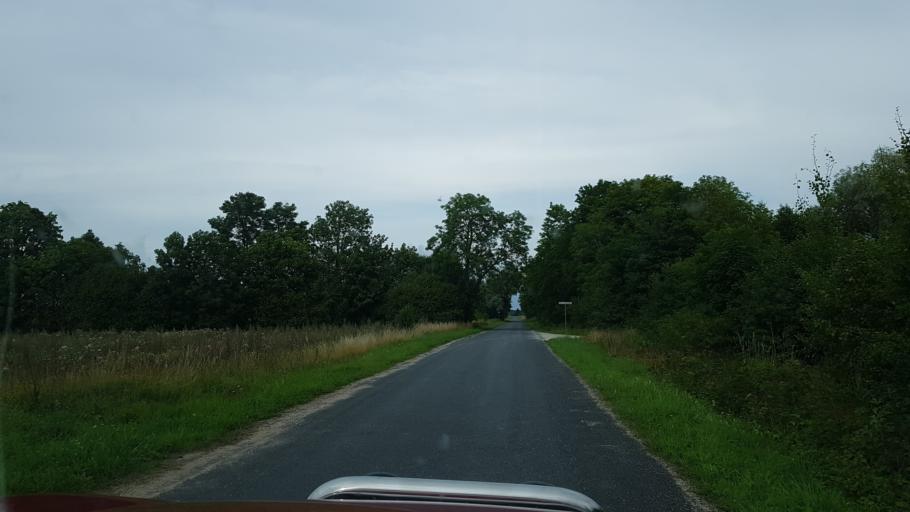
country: EE
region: Laeaene
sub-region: Ridala Parish
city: Uuemoisa
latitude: 58.9777
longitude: 23.7852
